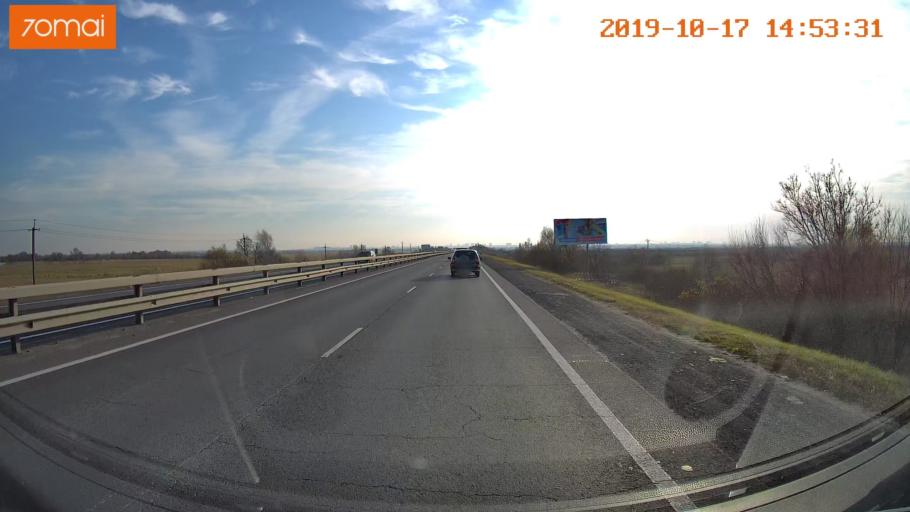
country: RU
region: Rjazan
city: Polyany
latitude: 54.6932
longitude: 39.8380
